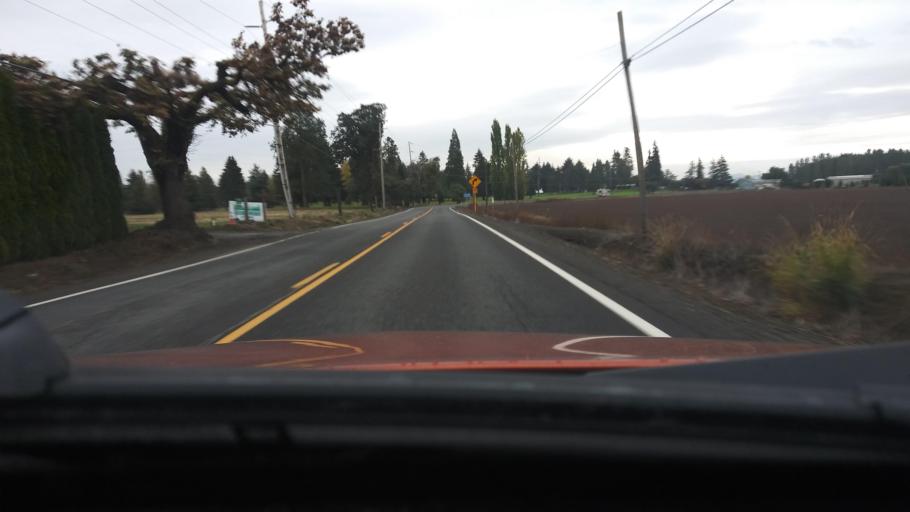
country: US
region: Oregon
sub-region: Washington County
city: Forest Grove
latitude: 45.5676
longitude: -123.1075
